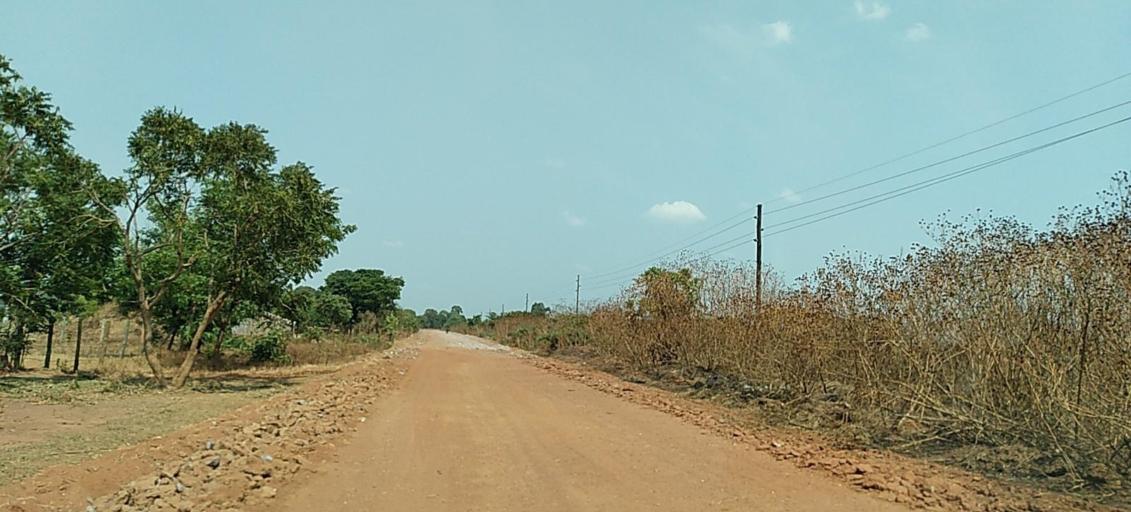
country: ZM
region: Copperbelt
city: Luanshya
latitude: -13.0939
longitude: 28.3133
